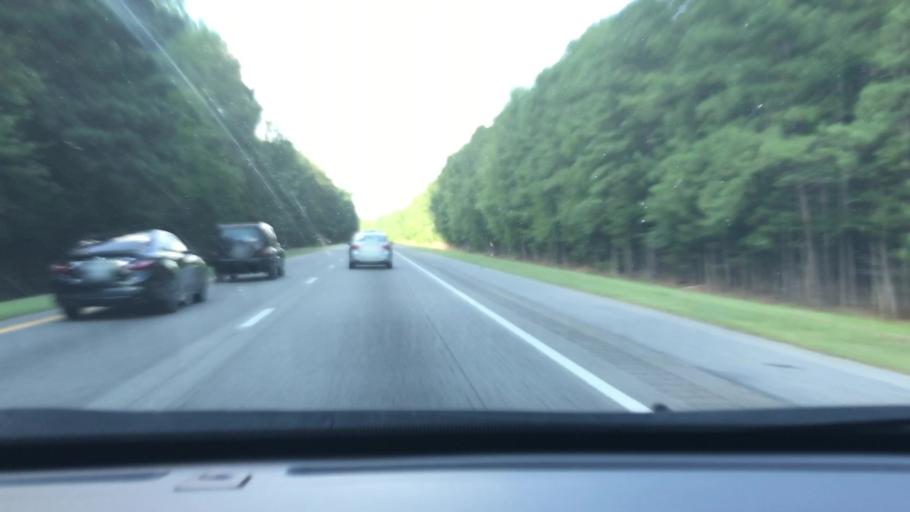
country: US
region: South Carolina
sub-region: Sumter County
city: East Sumter
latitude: 33.9233
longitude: -80.0758
